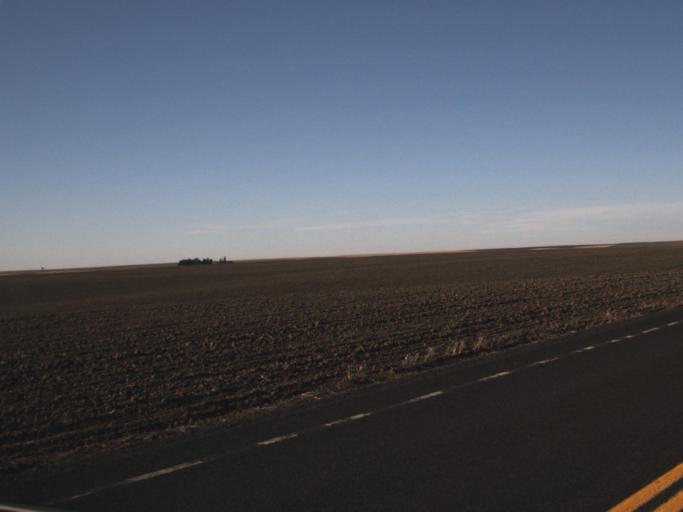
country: US
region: Washington
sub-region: Adams County
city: Ritzville
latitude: 46.9198
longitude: -118.3434
